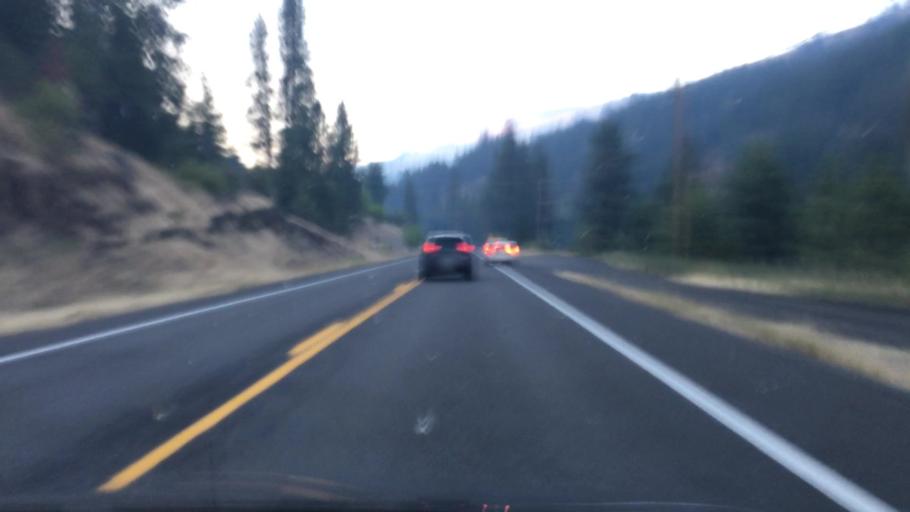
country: US
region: Idaho
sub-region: Valley County
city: McCall
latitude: 45.2078
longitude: -116.3131
